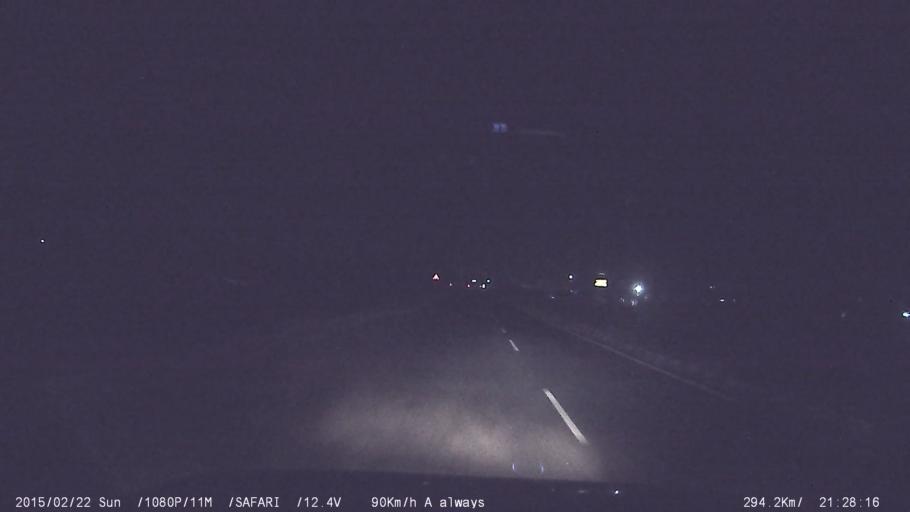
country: IN
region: Tamil Nadu
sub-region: Karur
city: Karur
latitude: 10.9240
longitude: 78.0472
